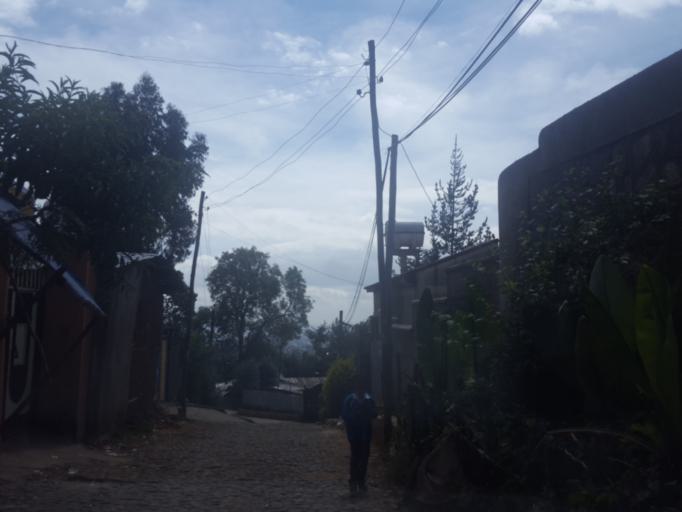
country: ET
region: Adis Abeba
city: Addis Ababa
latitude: 9.0648
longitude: 38.7425
